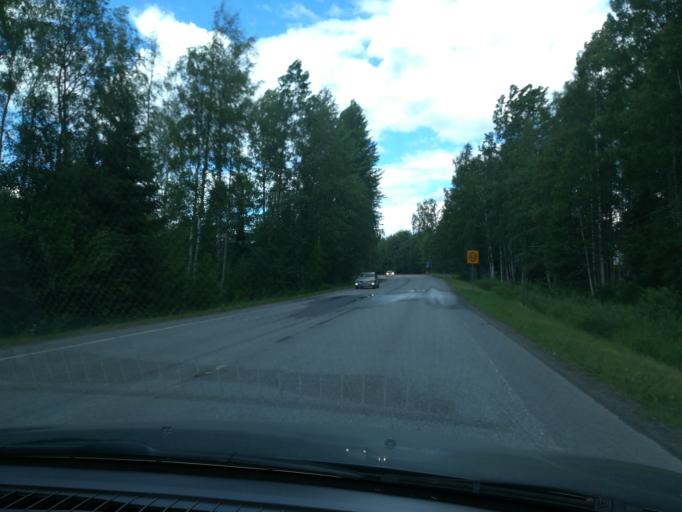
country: FI
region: Southern Savonia
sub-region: Mikkeli
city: Maentyharju
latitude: 61.4102
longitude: 26.8853
